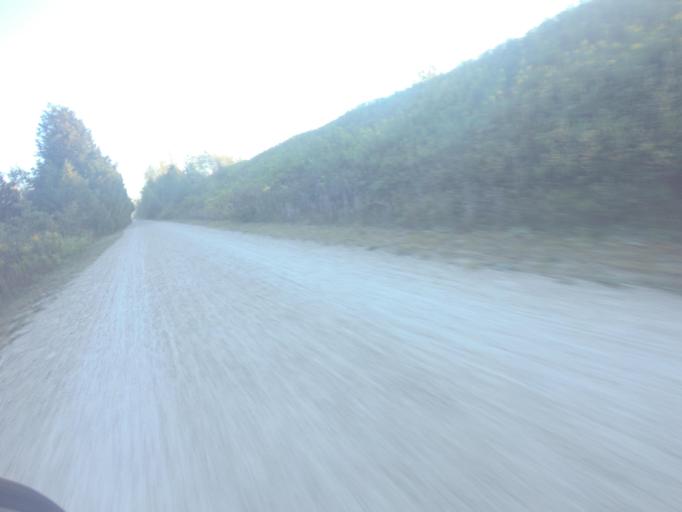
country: CA
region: Ontario
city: Bradford West Gwillimbury
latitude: 43.9772
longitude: -79.8066
